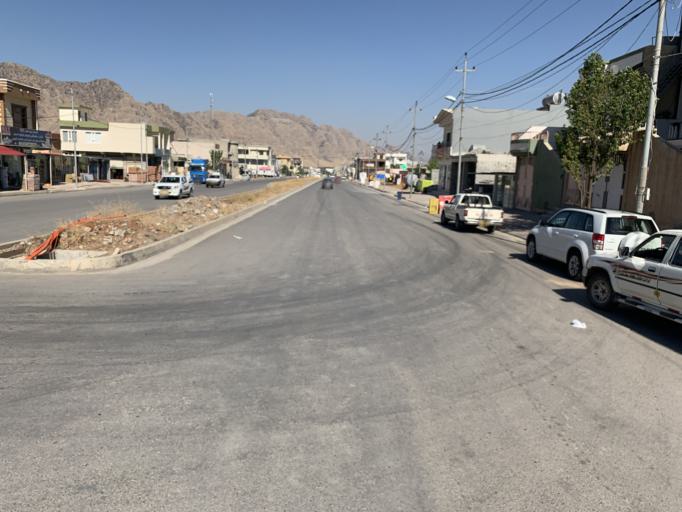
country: IQ
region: As Sulaymaniyah
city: Raniye
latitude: 36.2590
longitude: 44.8650
